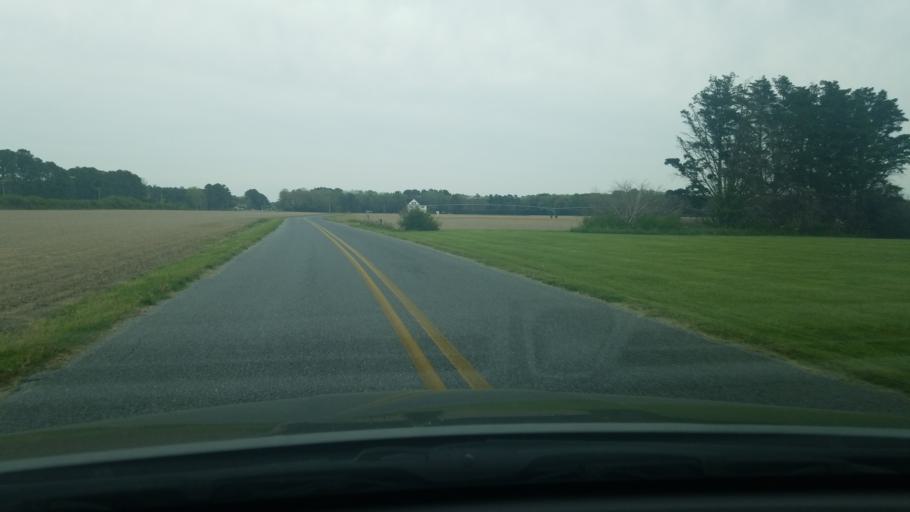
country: US
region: Maryland
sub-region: Worcester County
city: Snow Hill
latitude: 38.2371
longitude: -75.3076
